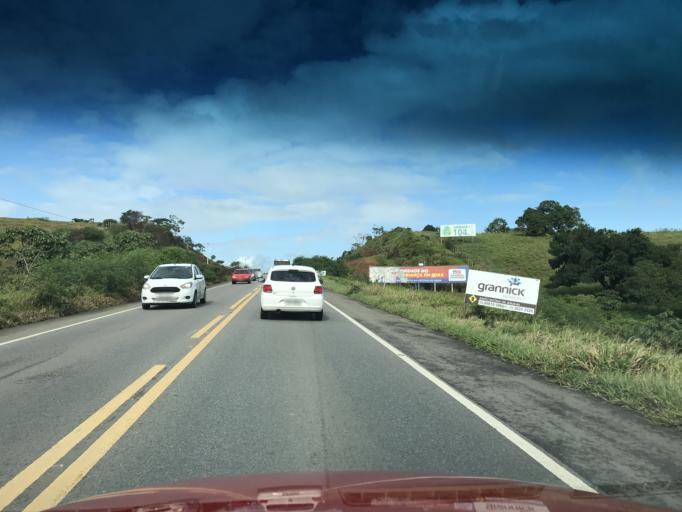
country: BR
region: Bahia
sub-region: Conceicao Do Almeida
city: Muritiba
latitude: -12.9105
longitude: -39.2408
